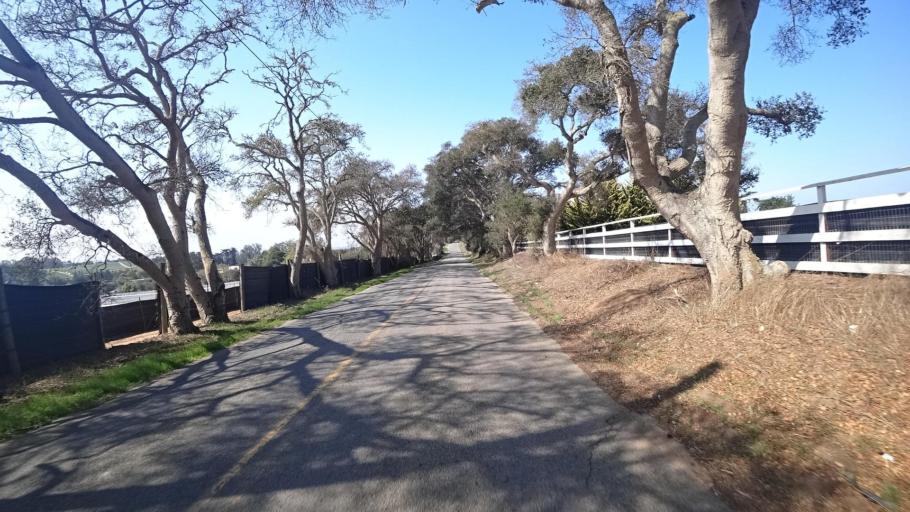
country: US
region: California
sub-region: Monterey County
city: Prunedale
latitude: 36.7893
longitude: -121.7111
